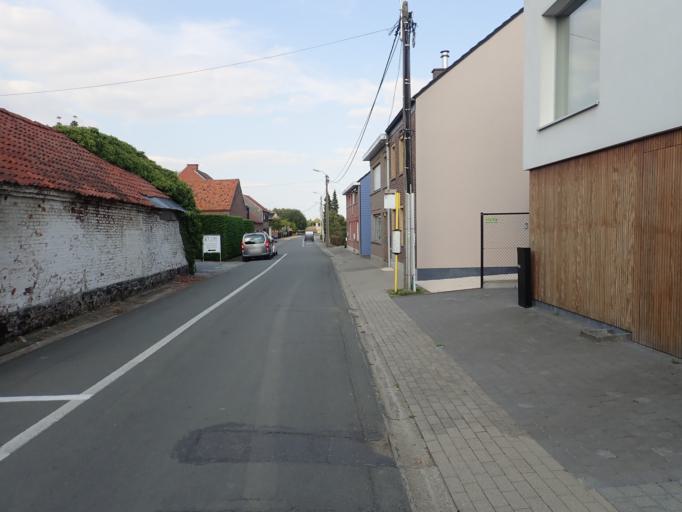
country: BE
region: Flanders
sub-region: Provincie Vlaams-Brabant
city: Opwijk
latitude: 50.9708
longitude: 4.2005
